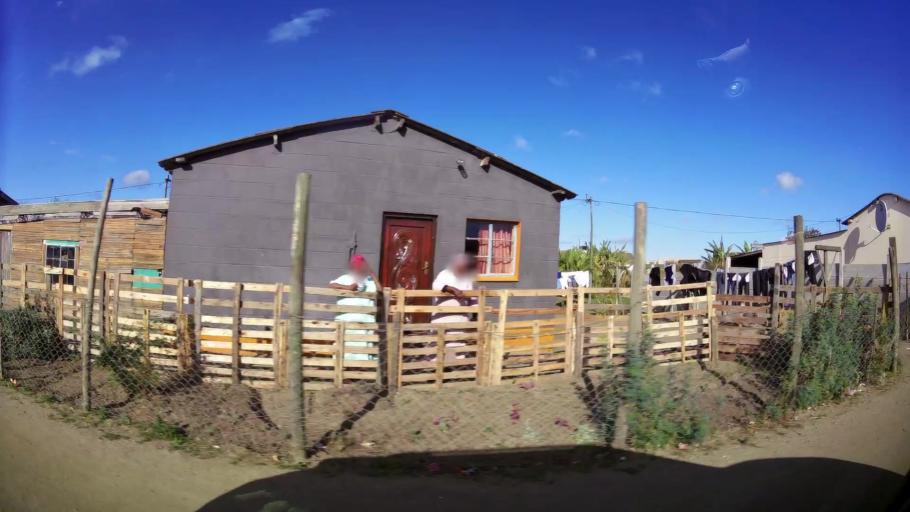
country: ZA
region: Western Cape
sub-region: Eden District Municipality
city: George
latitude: -33.9790
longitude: 22.4811
